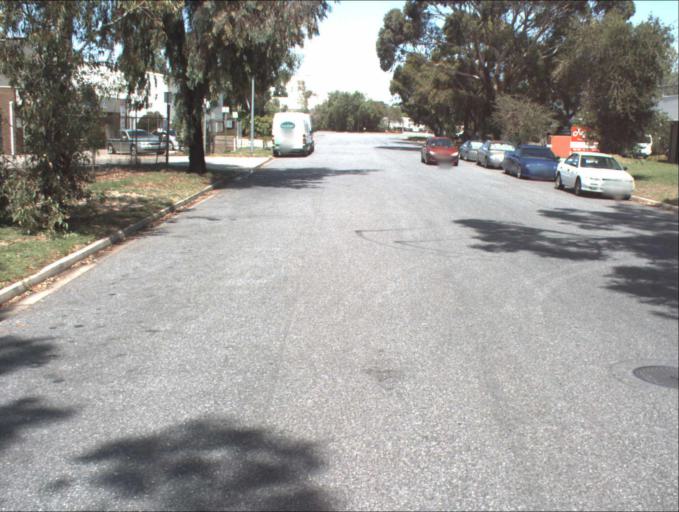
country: AU
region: South Australia
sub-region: Port Adelaide Enfield
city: Blair Athol
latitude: -34.8519
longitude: 138.5673
